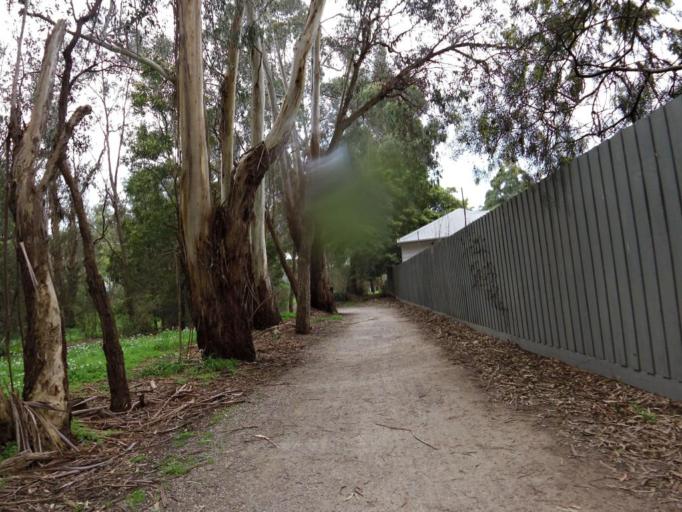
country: AU
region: Victoria
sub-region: Maroondah
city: Ringwood East
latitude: -37.8094
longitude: 145.2337
